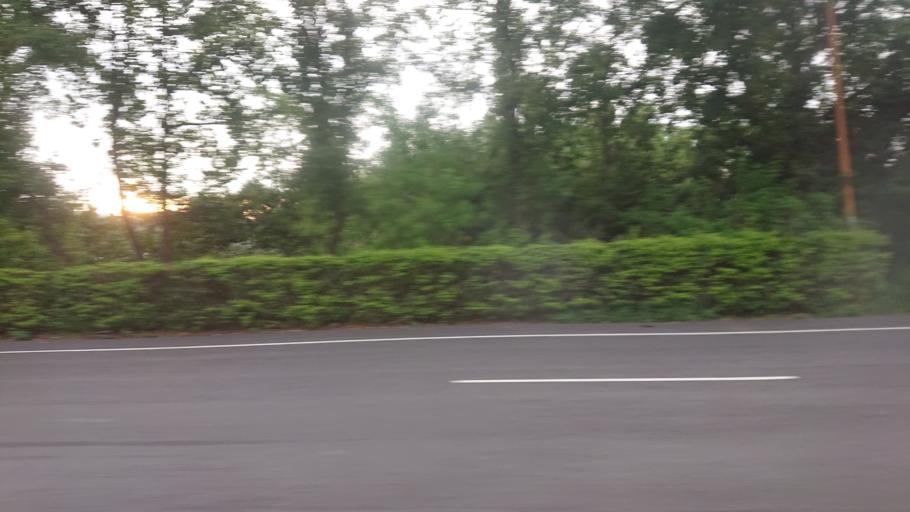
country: TW
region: Taiwan
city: Daxi
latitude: 24.8773
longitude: 121.2544
